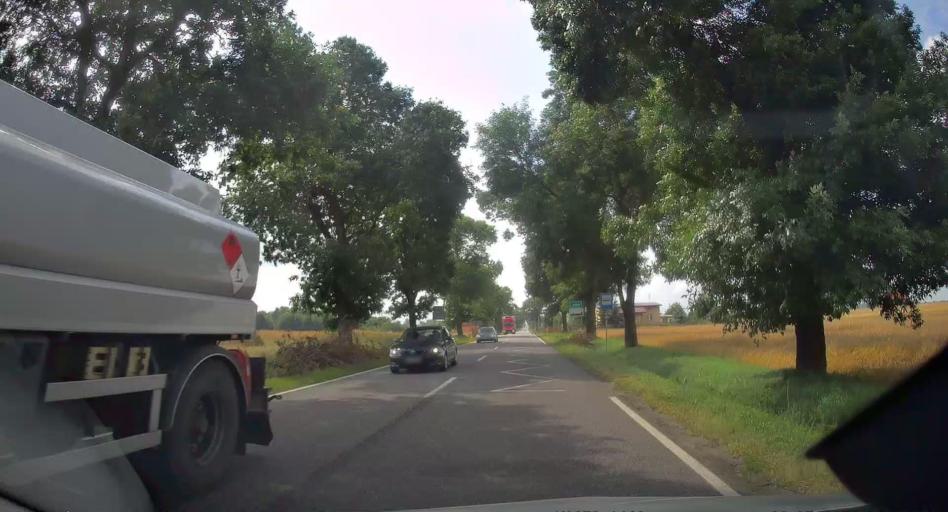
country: PL
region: Lodz Voivodeship
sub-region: Powiat brzezinski
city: Jezow
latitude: 51.8108
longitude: 19.9917
